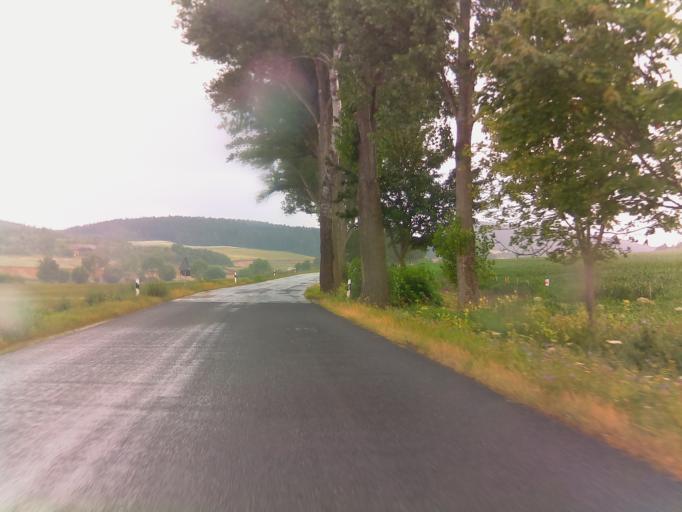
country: DE
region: Thuringia
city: Stadtilm
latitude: 50.7482
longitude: 11.1054
